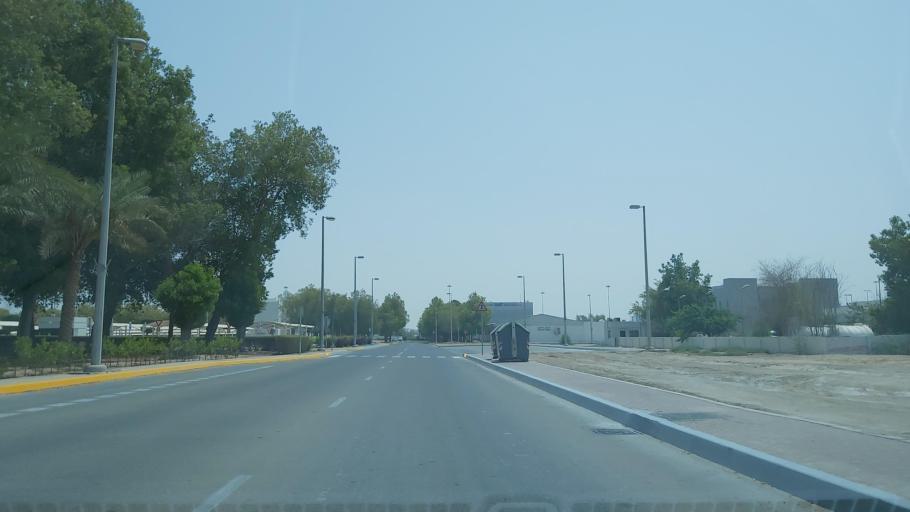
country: AE
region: Abu Dhabi
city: Abu Dhabi
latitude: 24.3793
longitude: 54.5205
